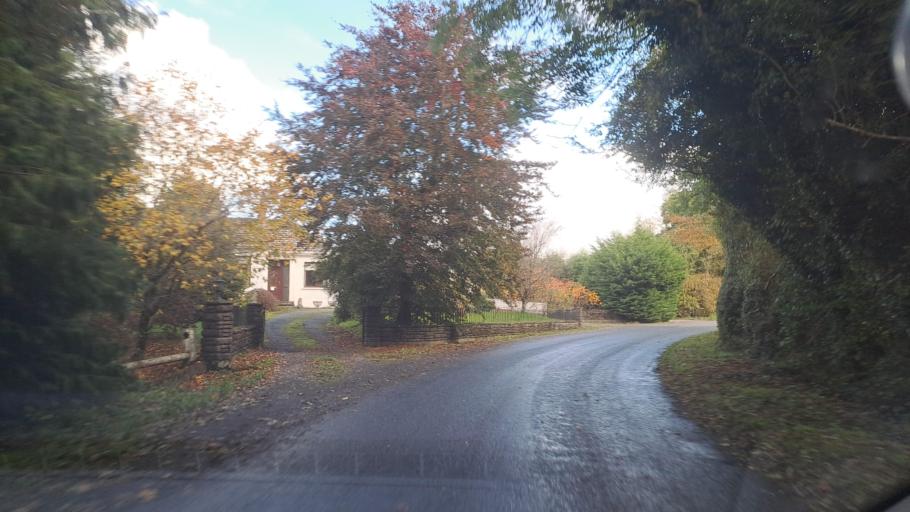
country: IE
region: Ulster
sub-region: An Cabhan
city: Bailieborough
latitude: 53.9911
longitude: -6.9915
